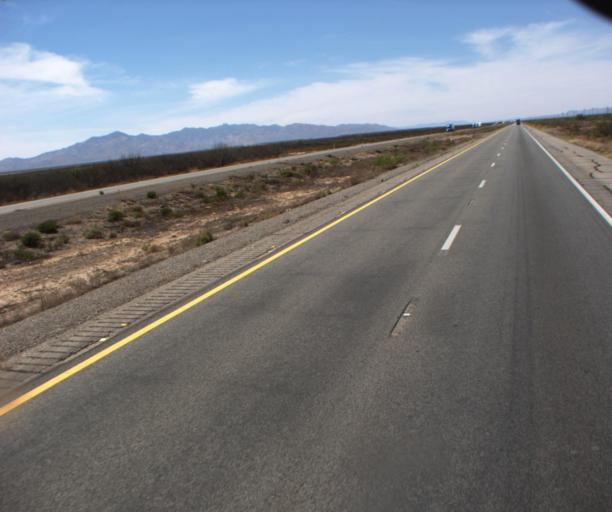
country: US
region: Arizona
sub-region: Cochise County
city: Willcox
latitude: 32.2800
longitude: -109.2776
